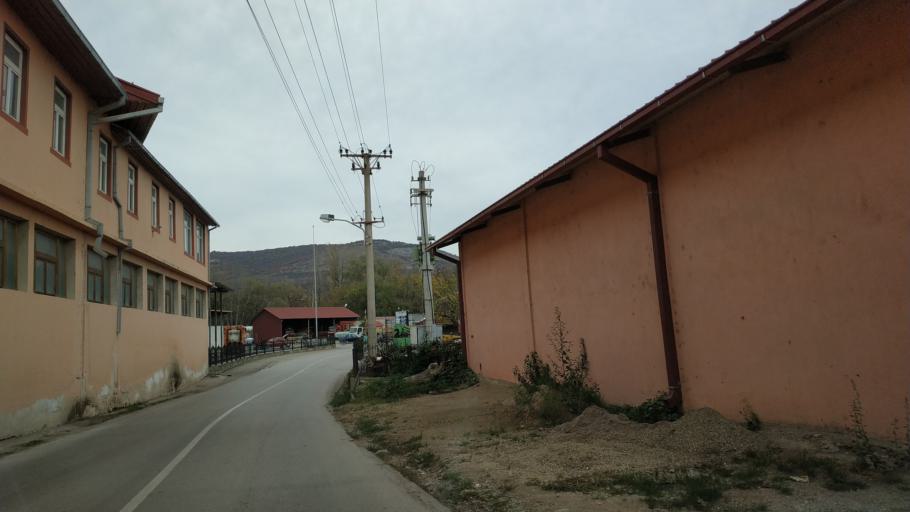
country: RS
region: Central Serbia
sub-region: Nisavski Okrug
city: Nis
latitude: 43.3569
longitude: 21.9500
